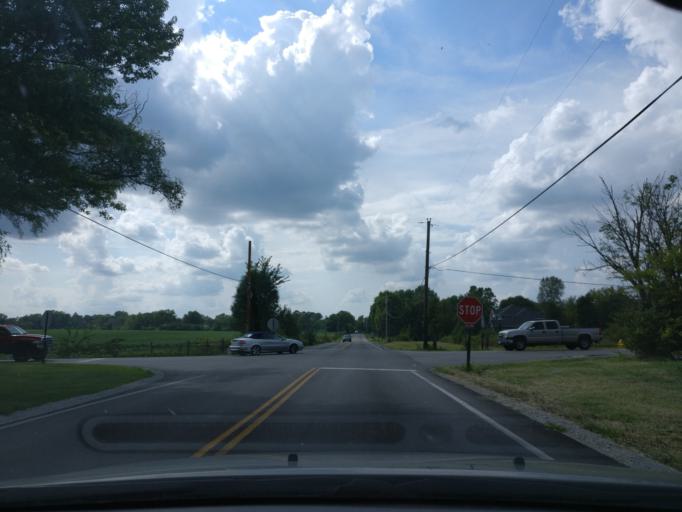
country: US
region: Ohio
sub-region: Greene County
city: Bellbrook
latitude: 39.6100
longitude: -84.1015
